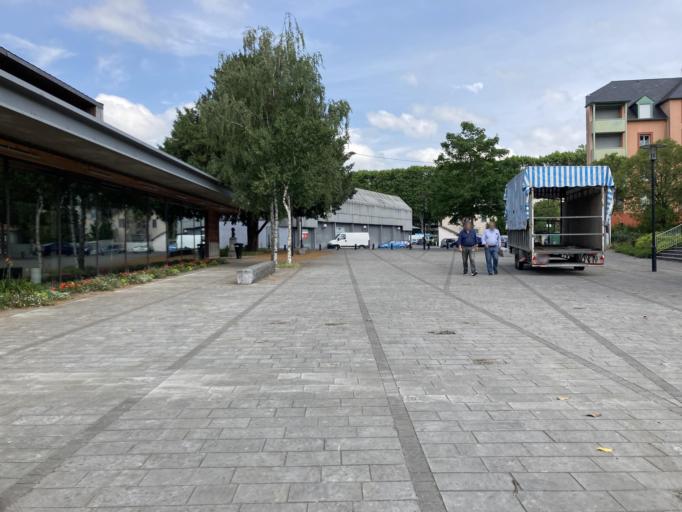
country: FR
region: Aquitaine
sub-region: Departement des Pyrenees-Atlantiques
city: Oloron-Sainte-Marie
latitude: 43.1903
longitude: -0.6108
